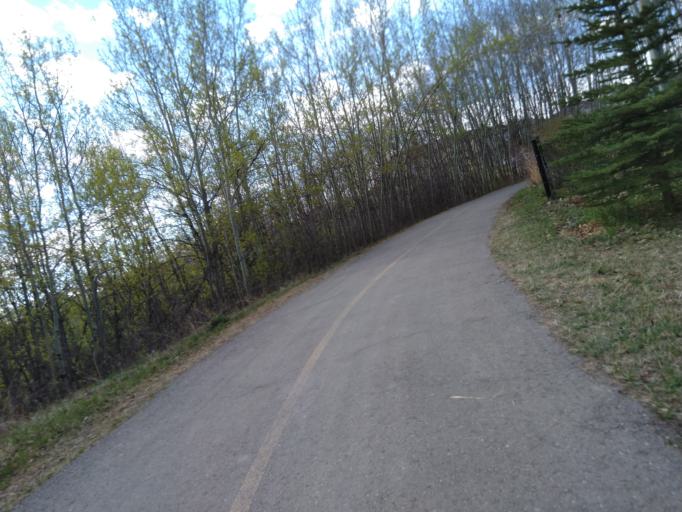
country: CA
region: Alberta
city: Calgary
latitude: 51.1185
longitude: -114.2368
